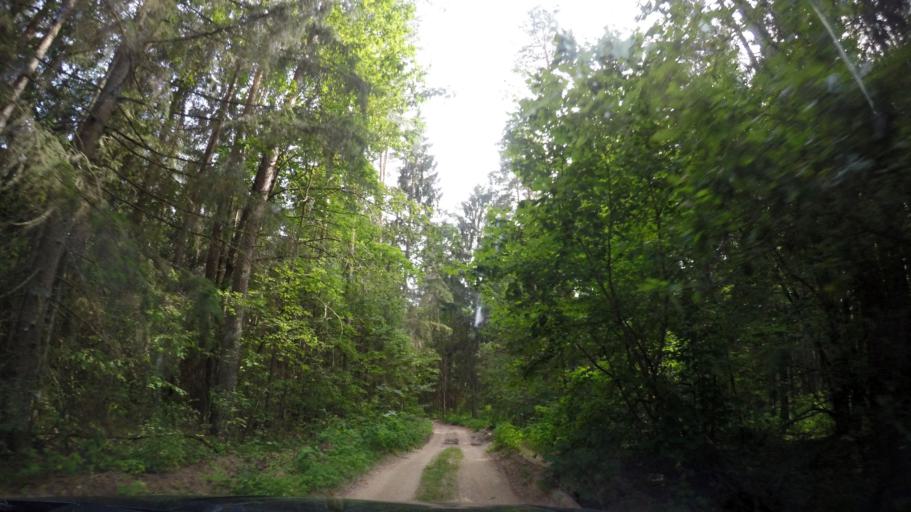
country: BY
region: Grodnenskaya
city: Skidal'
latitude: 53.8352
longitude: 24.1767
